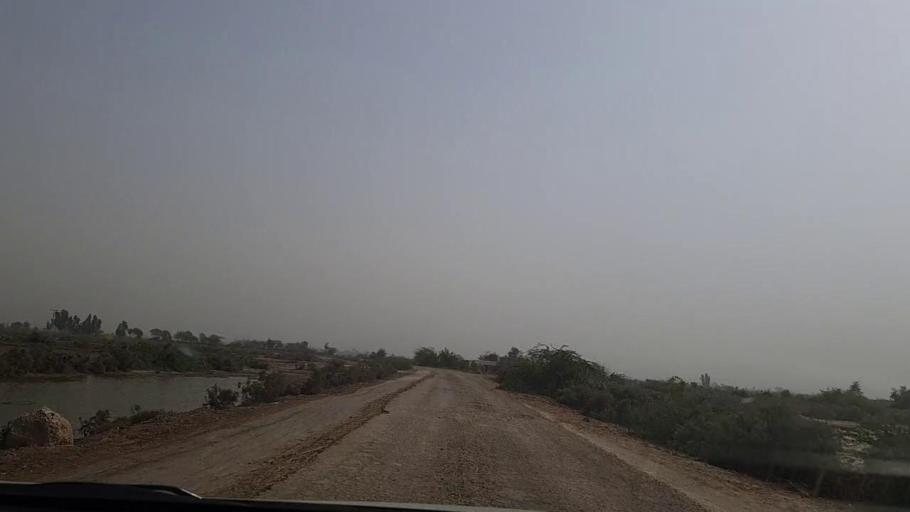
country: PK
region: Sindh
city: Pithoro
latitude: 25.4635
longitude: 69.2280
